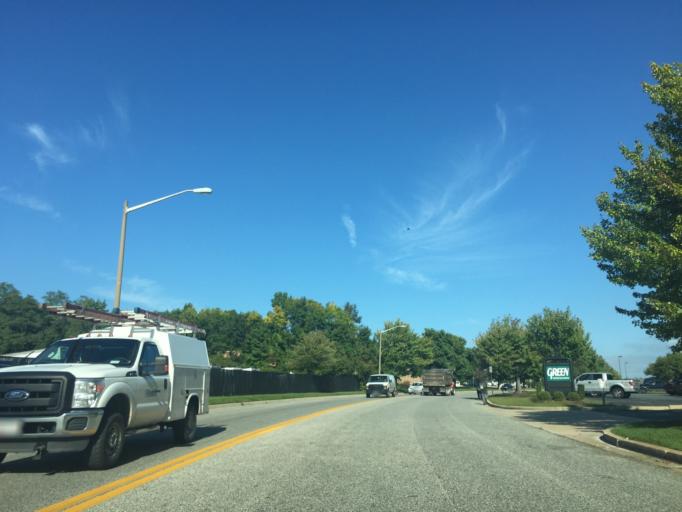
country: US
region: Maryland
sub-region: Baltimore County
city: Rossville
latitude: 39.3404
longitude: -76.4813
